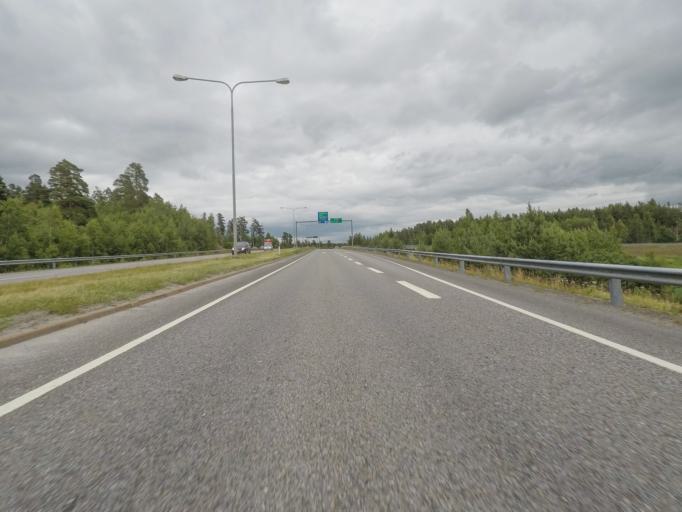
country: FI
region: Varsinais-Suomi
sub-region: Turku
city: Piikkioe
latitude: 60.4441
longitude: 22.4861
